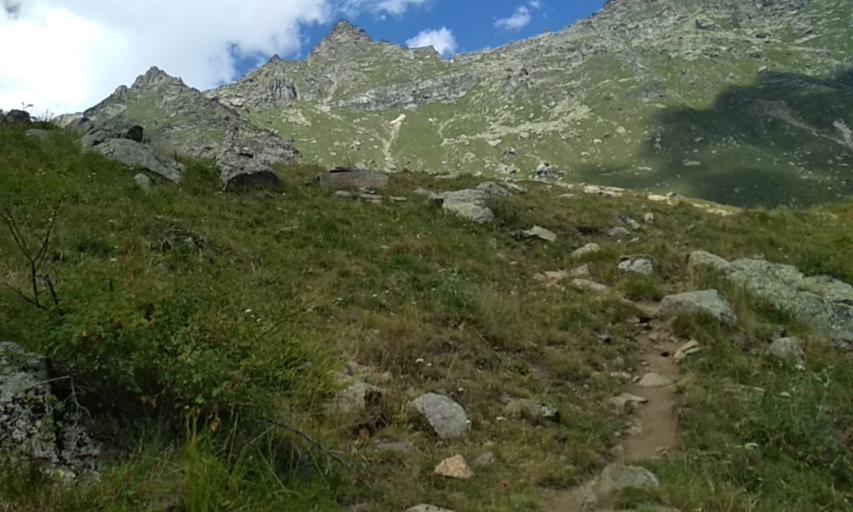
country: IT
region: Piedmont
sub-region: Provincia di Torino
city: Noasca
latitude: 45.4616
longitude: 7.2975
